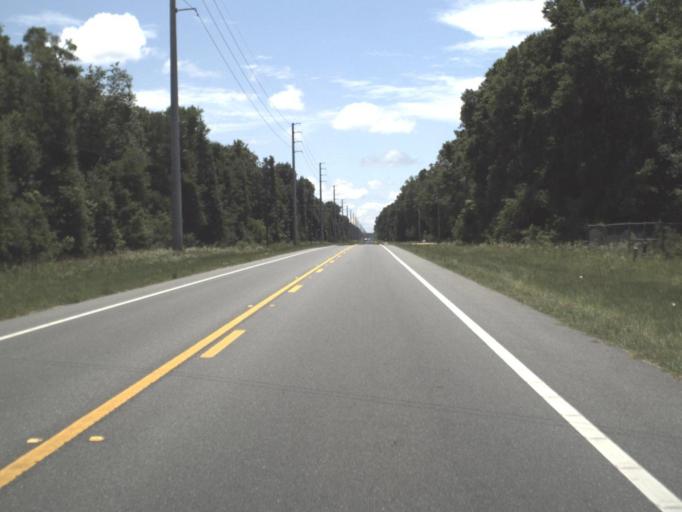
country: US
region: Florida
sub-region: Dixie County
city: Cross City
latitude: 29.6465
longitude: -82.9837
